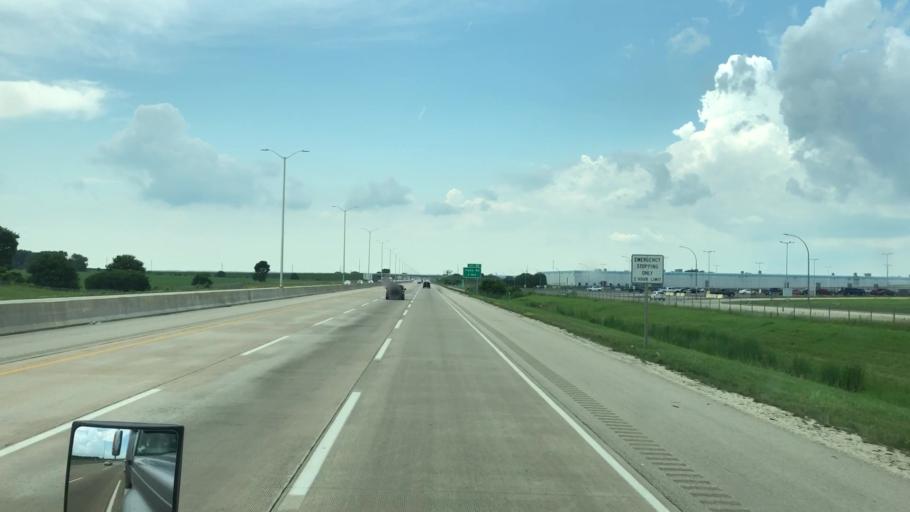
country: US
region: Illinois
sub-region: Boone County
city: Belvidere
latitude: 42.2335
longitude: -88.8705
